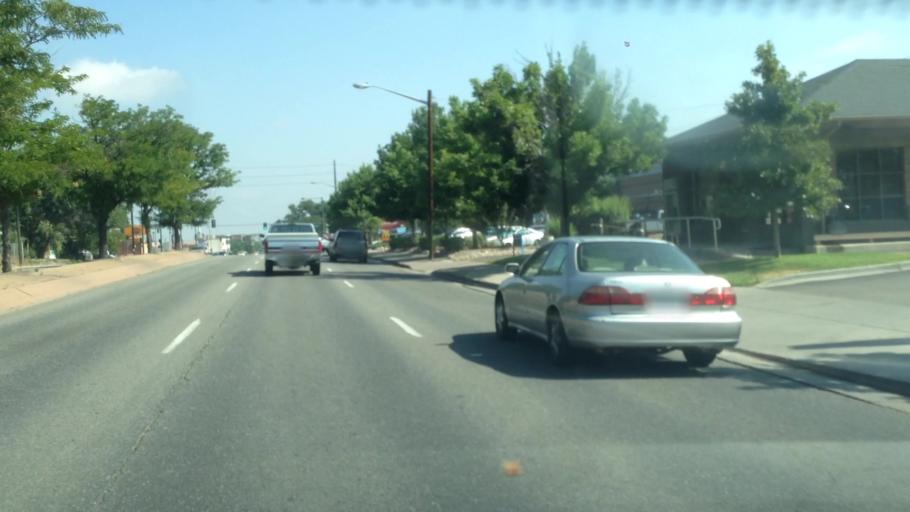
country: US
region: Colorado
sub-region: Adams County
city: Commerce City
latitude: 39.7629
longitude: -104.9405
